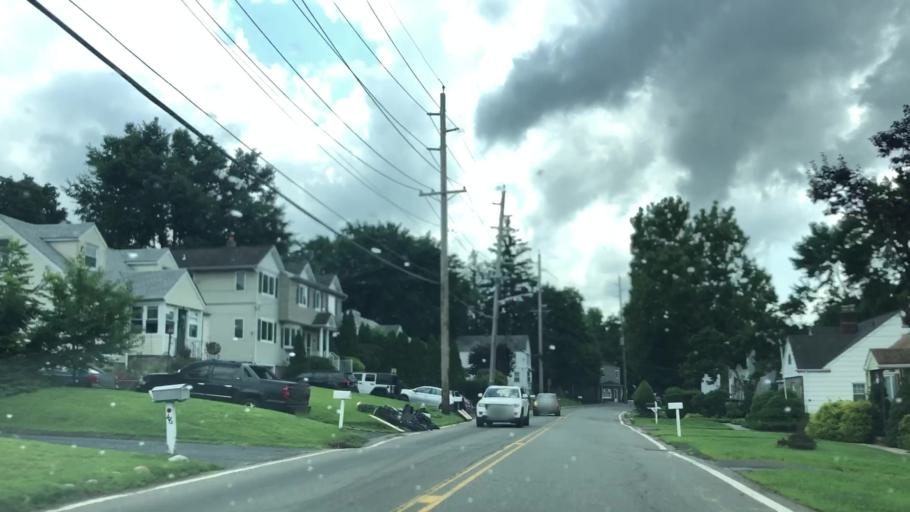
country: US
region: New Jersey
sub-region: Passaic County
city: Little Falls
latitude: 40.8781
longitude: -74.2146
